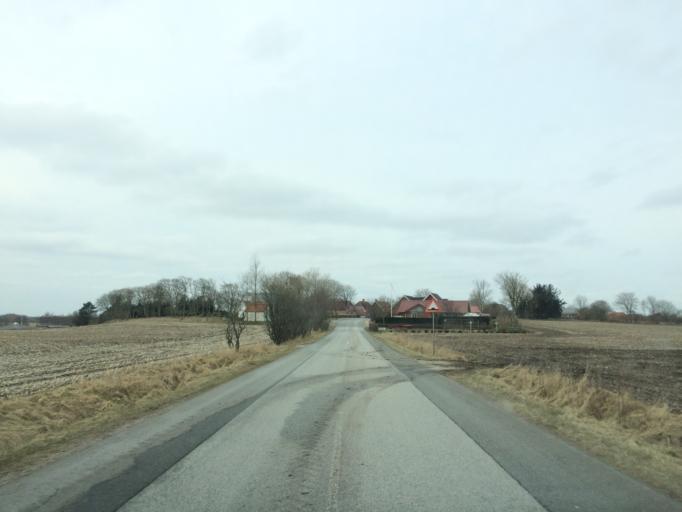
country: DK
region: South Denmark
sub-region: Varde Kommune
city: Oksbol
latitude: 55.7965
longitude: 8.3648
